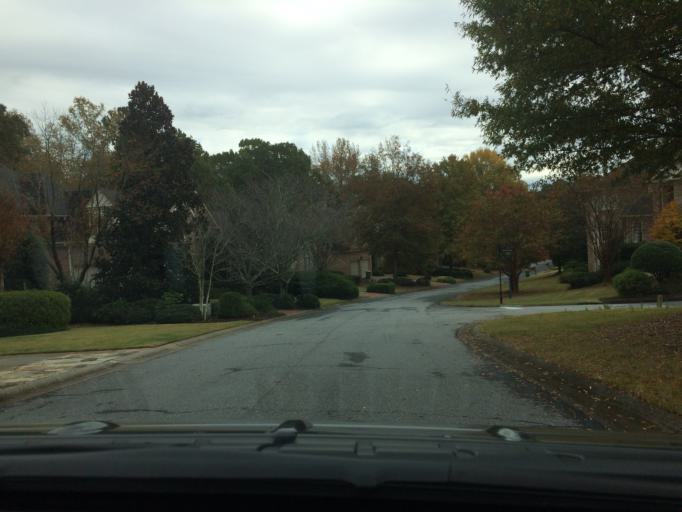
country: US
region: Georgia
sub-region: Fulton County
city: Johns Creek
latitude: 34.0093
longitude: -84.2488
